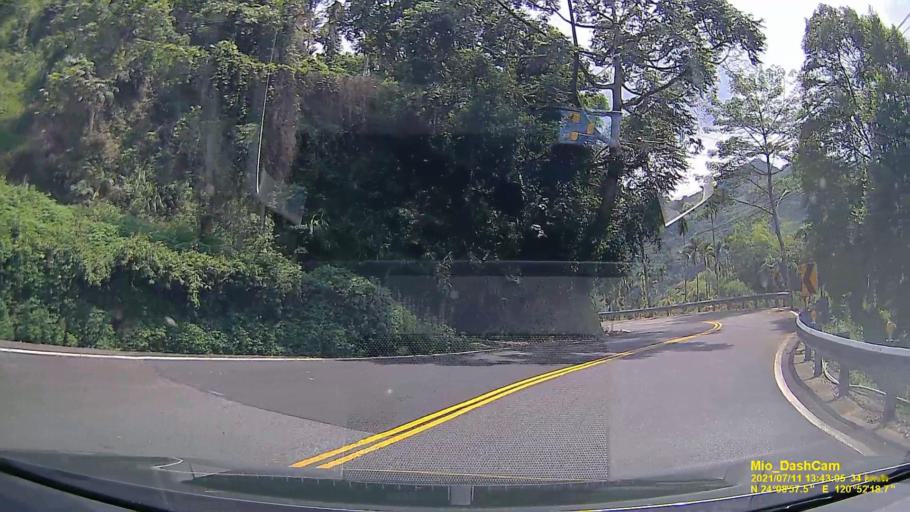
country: TW
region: Taiwan
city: Fengyuan
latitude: 24.1492
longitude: 120.8719
